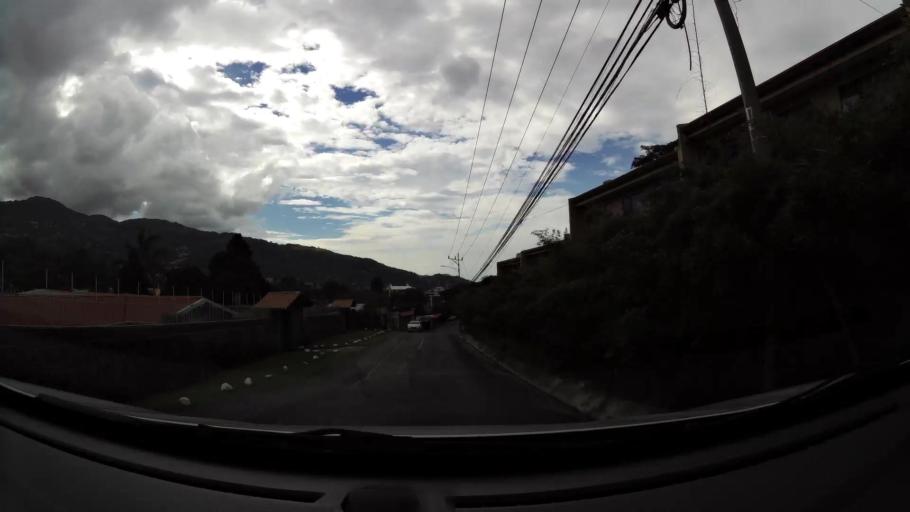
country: CR
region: San Jose
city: San Rafael
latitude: 9.9216
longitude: -84.1312
